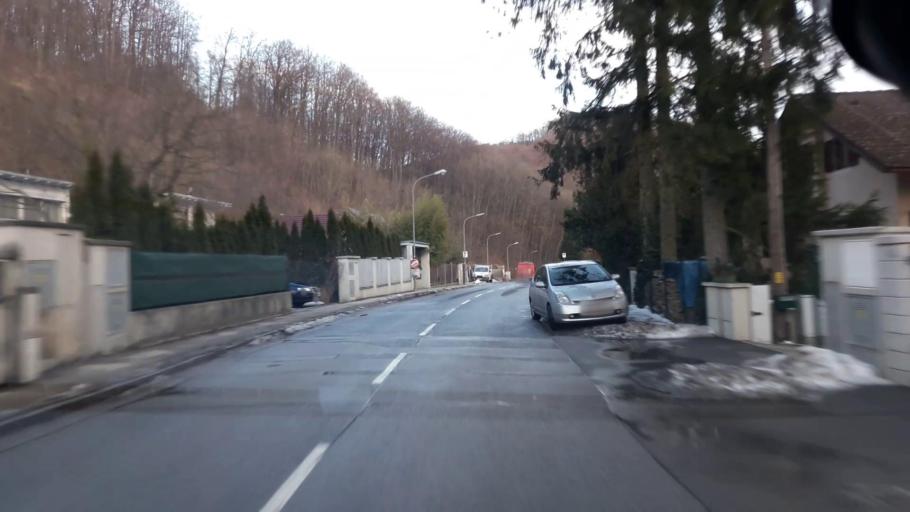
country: AT
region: Lower Austria
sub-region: Politischer Bezirk Wien-Umgebung
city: Klosterneuburg
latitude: 48.2673
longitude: 16.2661
